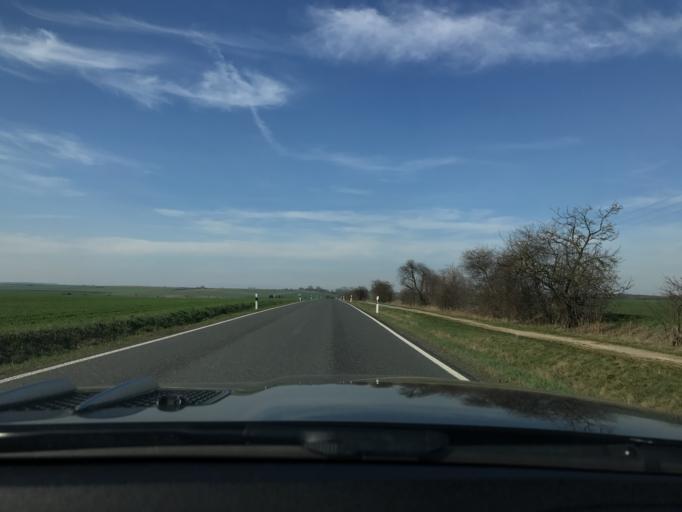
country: DE
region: Thuringia
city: Bothenheilingen
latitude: 51.1516
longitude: 10.6354
